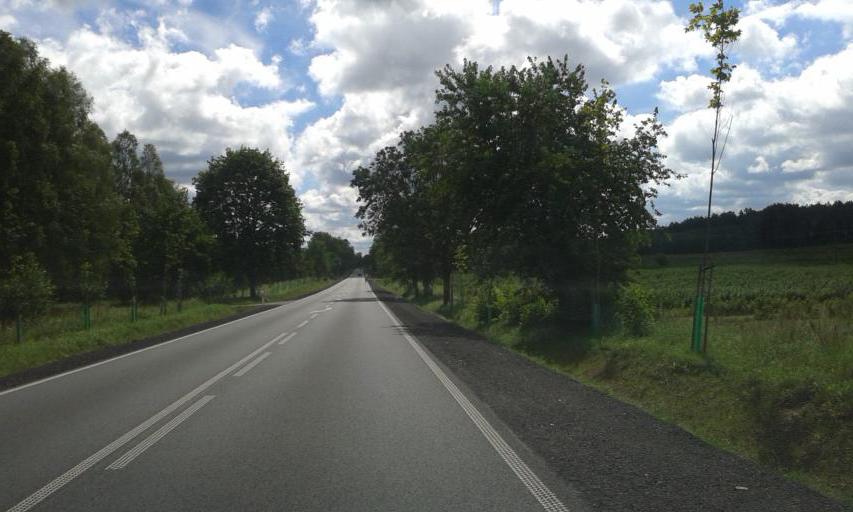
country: PL
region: West Pomeranian Voivodeship
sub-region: Powiat drawski
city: Czaplinek
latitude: 53.5344
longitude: 16.2846
